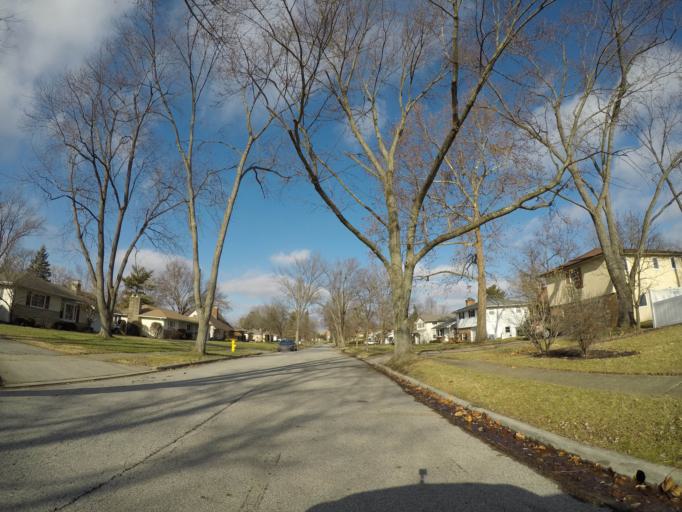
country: US
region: Ohio
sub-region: Franklin County
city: Upper Arlington
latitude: 40.0276
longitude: -83.0638
